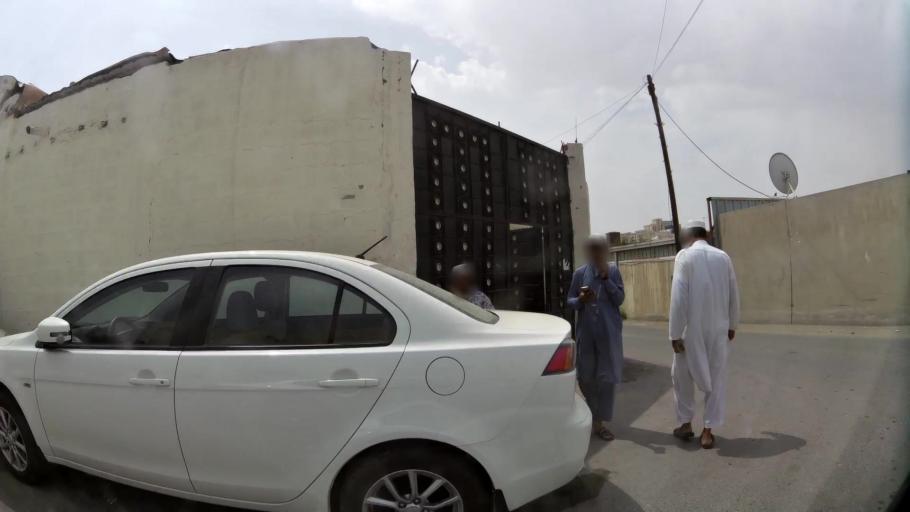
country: QA
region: Baladiyat ad Dawhah
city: Doha
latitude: 25.2772
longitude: 51.5202
